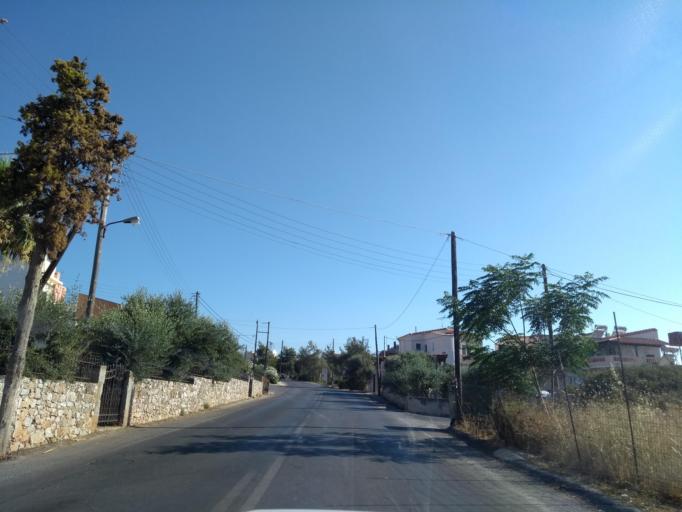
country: GR
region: Crete
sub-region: Nomos Chanias
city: Pithari
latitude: 35.5480
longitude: 24.0832
